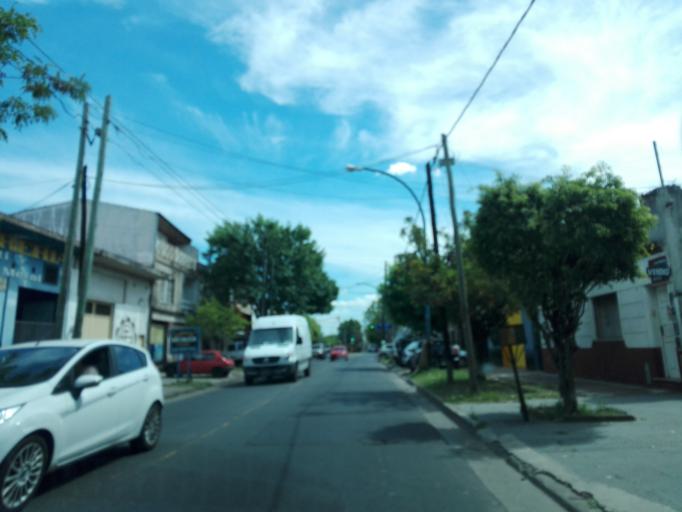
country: AR
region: Buenos Aires
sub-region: Partido de Lanus
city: Lanus
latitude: -34.7105
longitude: -58.3762
